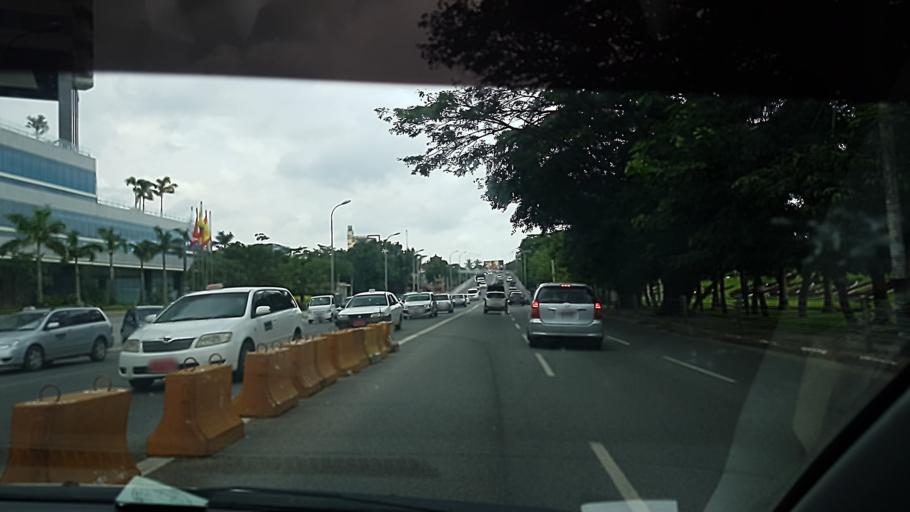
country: MM
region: Yangon
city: Yangon
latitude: 16.8272
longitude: 96.1543
